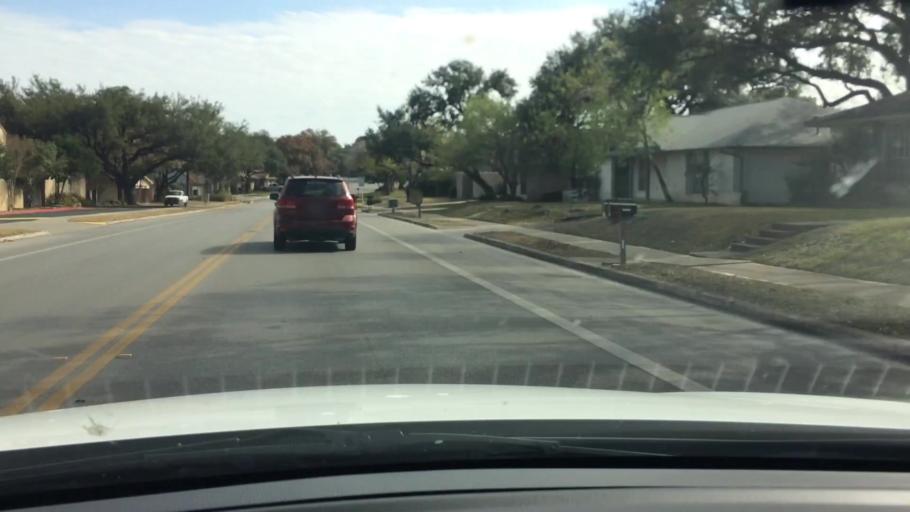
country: US
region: Texas
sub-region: Bexar County
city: Hollywood Park
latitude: 29.5777
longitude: -98.4720
